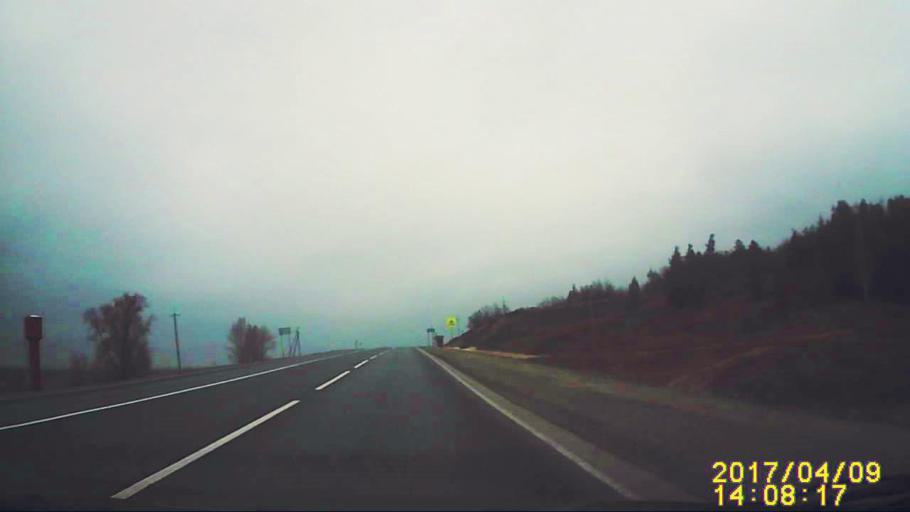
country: RU
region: Ulyanovsk
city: Silikatnyy
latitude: 54.0189
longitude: 48.2159
